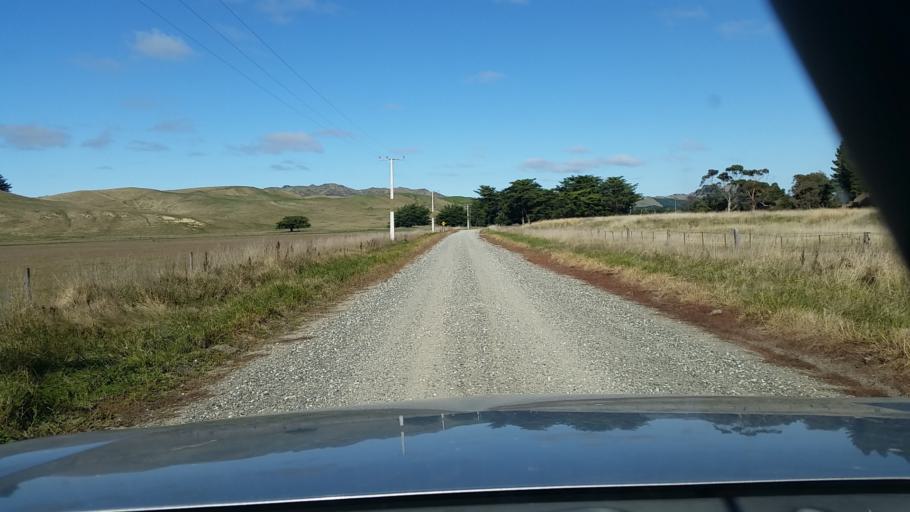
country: NZ
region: Marlborough
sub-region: Marlborough District
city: Blenheim
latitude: -41.7410
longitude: 174.1551
